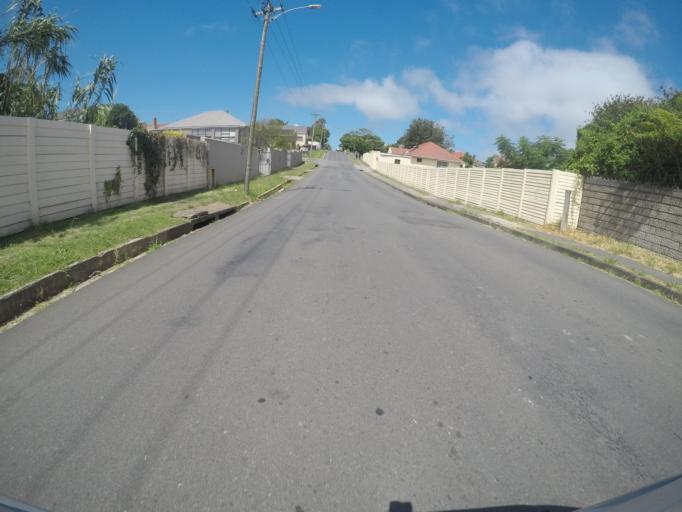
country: ZA
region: Eastern Cape
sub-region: Buffalo City Metropolitan Municipality
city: East London
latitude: -32.9776
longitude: 27.8906
